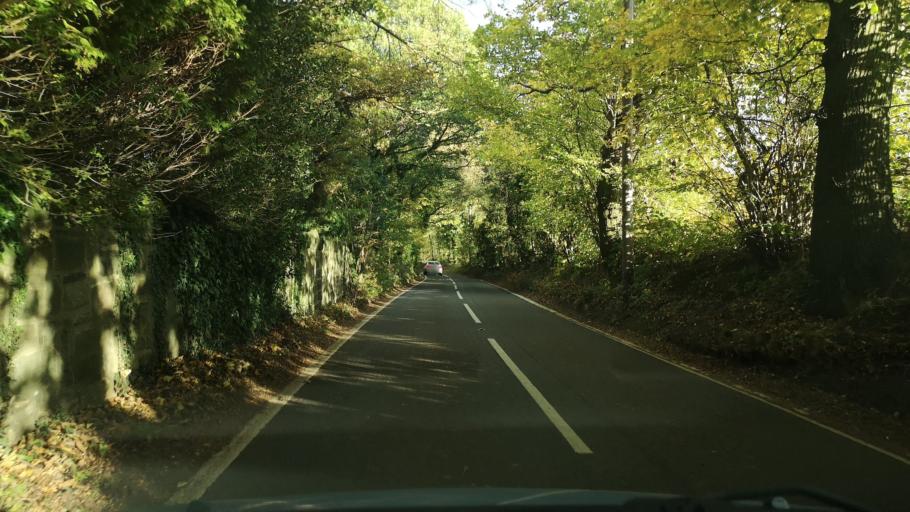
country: GB
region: England
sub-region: City and Borough of Wakefield
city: Woolley
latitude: 53.6214
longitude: -1.5047
